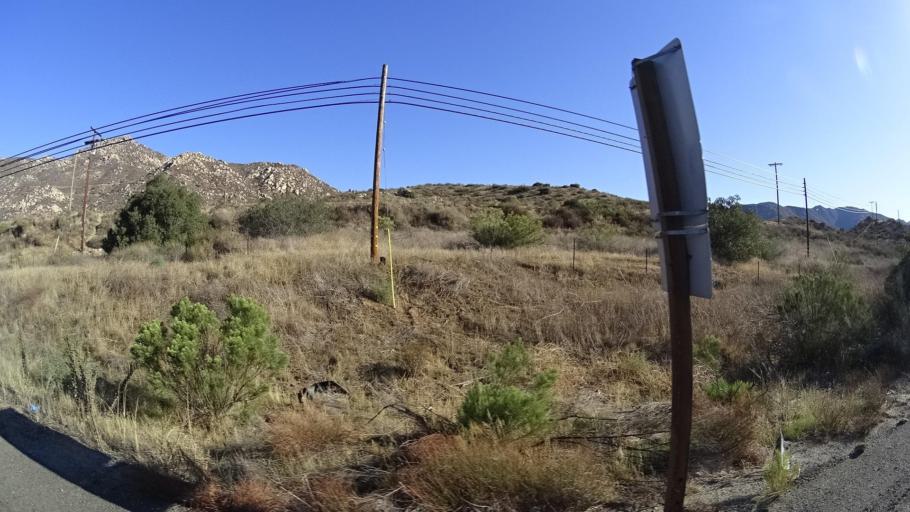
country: MX
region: Baja California
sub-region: Tecate
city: Lomas de Santa Anita
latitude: 32.6103
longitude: -116.7024
